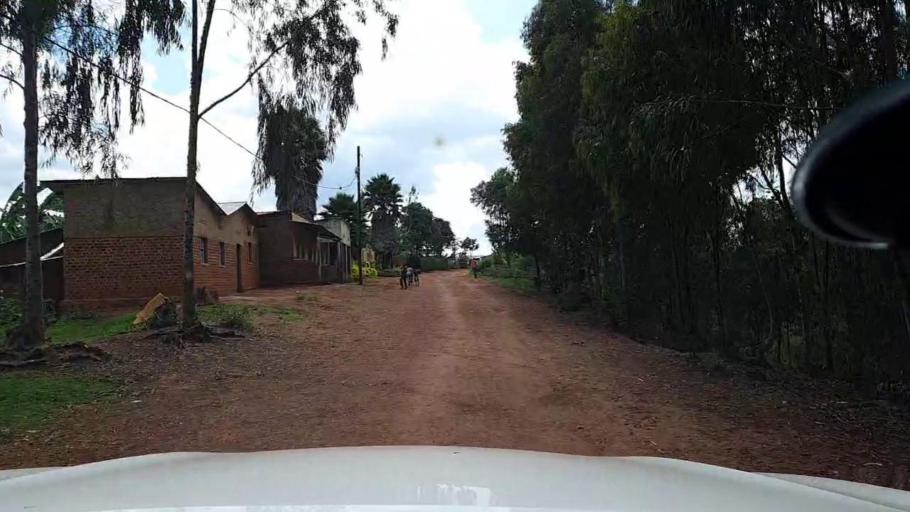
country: RW
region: Southern Province
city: Gitarama
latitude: -1.8369
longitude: 29.8329
